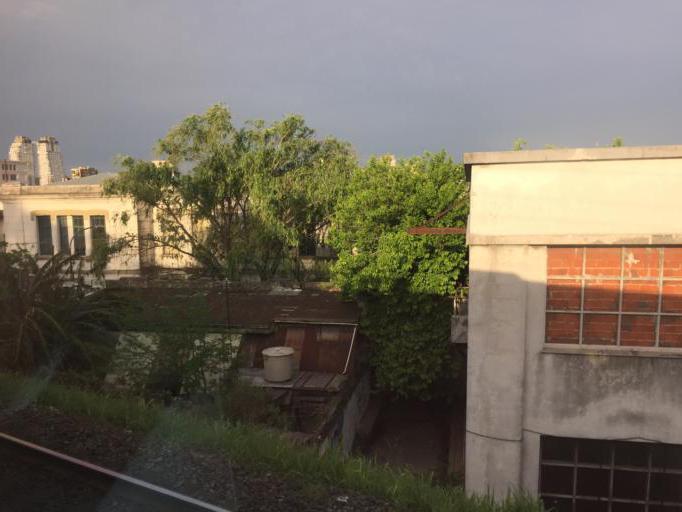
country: AR
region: Buenos Aires
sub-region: Partido de Avellaneda
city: Avellaneda
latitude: -34.6415
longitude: -58.3807
